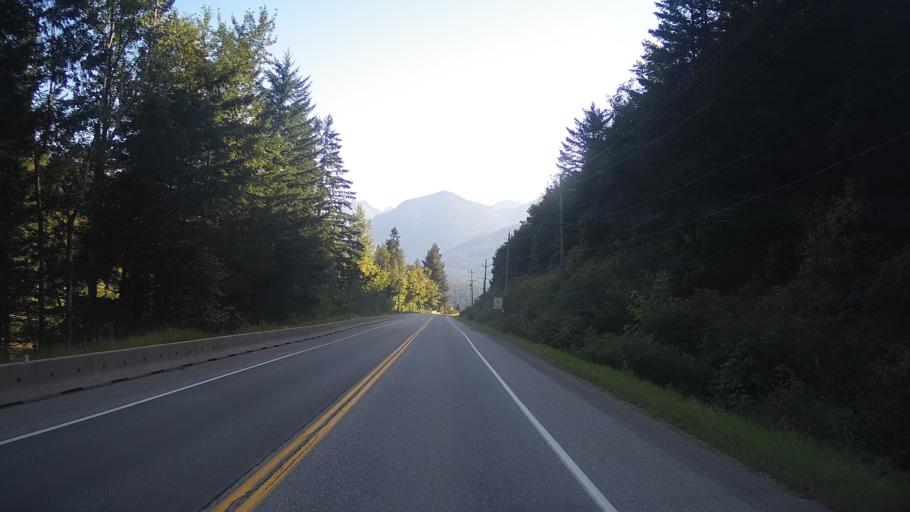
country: CA
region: British Columbia
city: Hope
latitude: 49.4111
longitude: -121.4432
